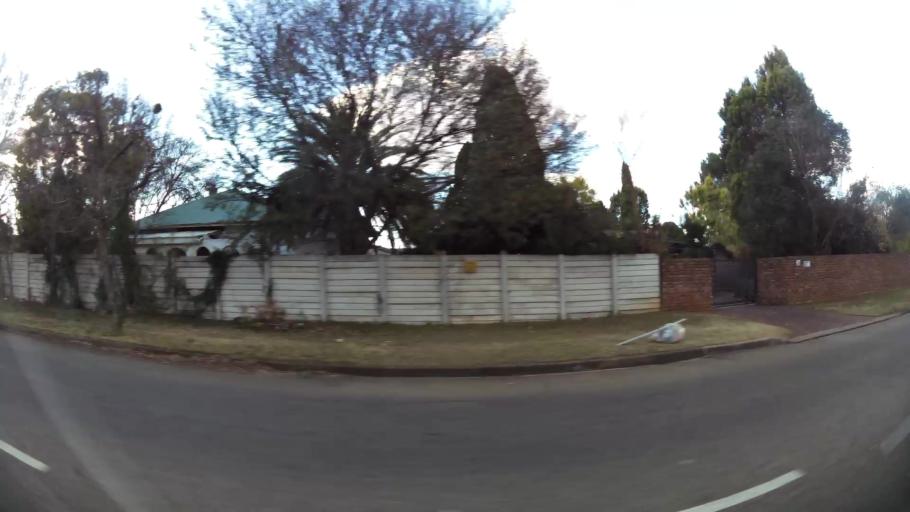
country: ZA
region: North-West
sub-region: Dr Kenneth Kaunda District Municipality
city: Potchefstroom
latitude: -26.7203
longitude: 27.0871
